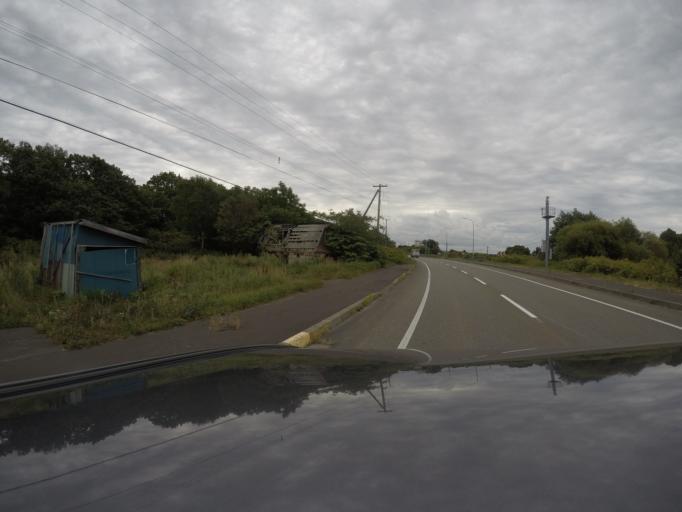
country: JP
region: Hokkaido
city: Makubetsu
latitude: 45.1454
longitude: 141.7518
